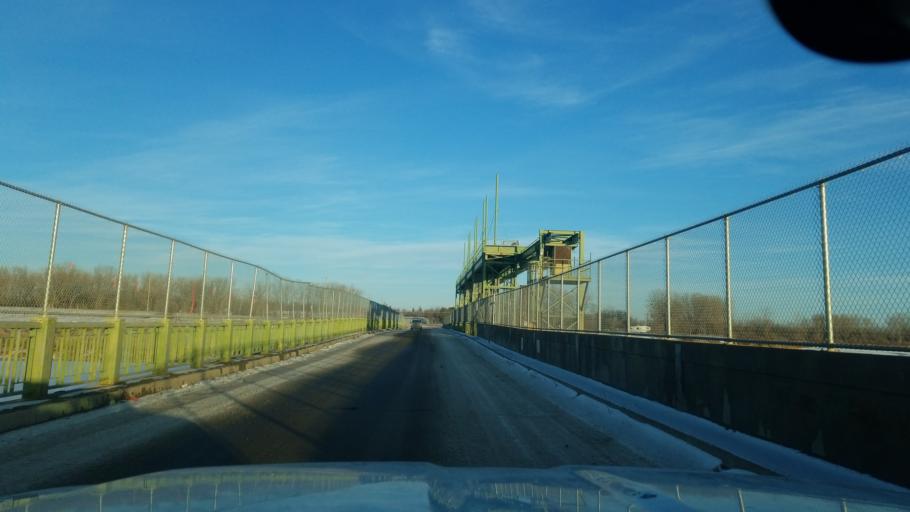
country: CA
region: Manitoba
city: Portage la Prairie
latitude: 49.9491
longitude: -98.3372
